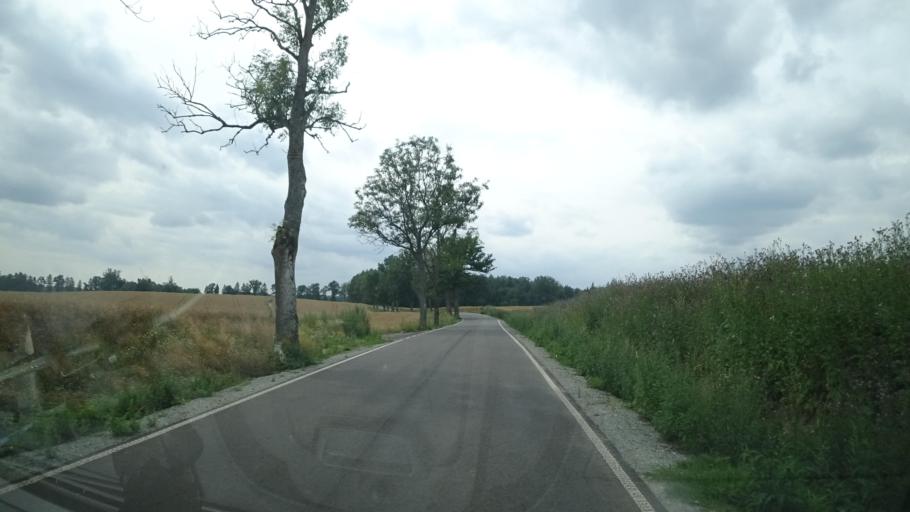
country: PL
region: Warmian-Masurian Voivodeship
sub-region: Powiat elblaski
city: Paslek
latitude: 53.9720
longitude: 19.6286
